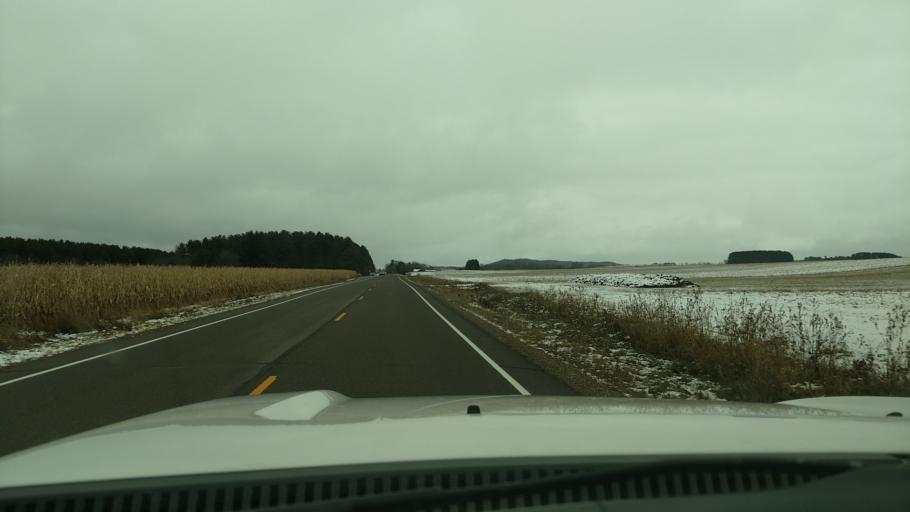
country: US
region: Wisconsin
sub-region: Dunn County
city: Colfax
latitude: 45.1426
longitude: -91.6751
